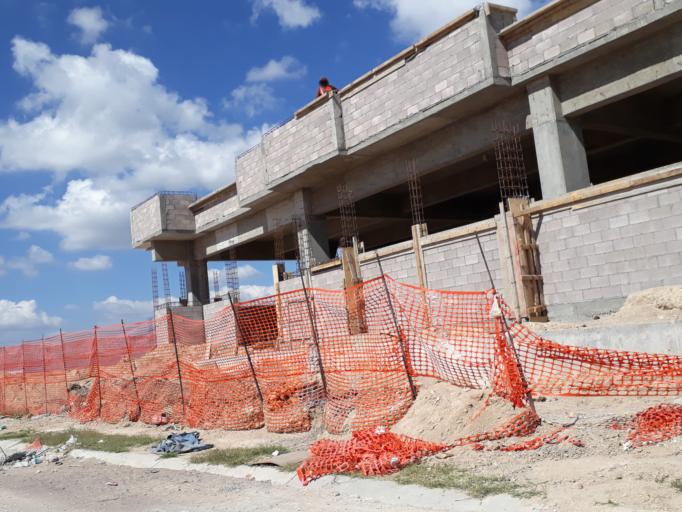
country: MX
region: Aguascalientes
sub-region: Aguascalientes
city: San Sebastian [Fraccionamiento]
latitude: 21.8091
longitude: -102.2861
